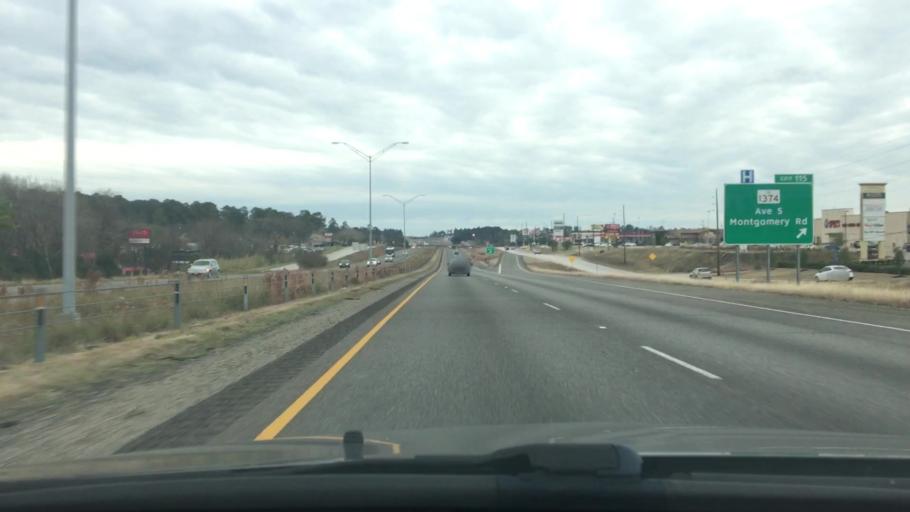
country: US
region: Texas
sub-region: Walker County
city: Huntsville
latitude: 30.7132
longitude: -95.5666
